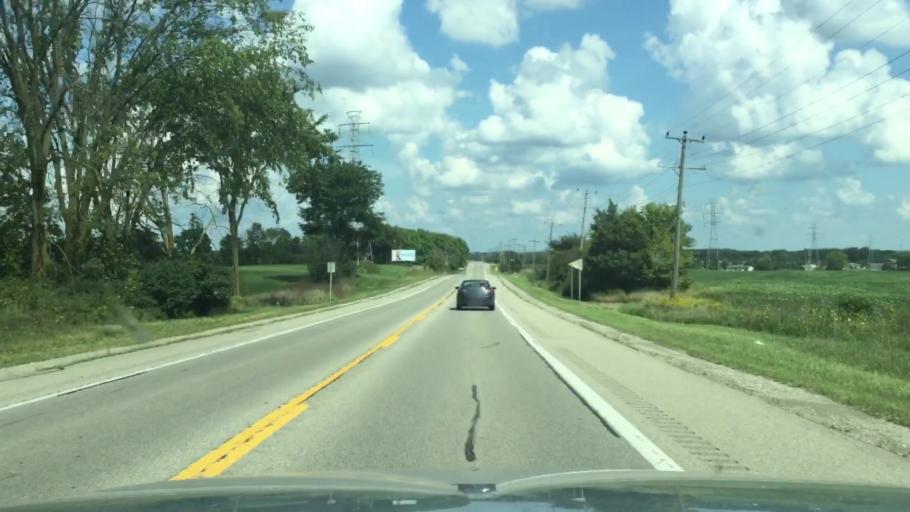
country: US
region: Michigan
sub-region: Washtenaw County
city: Saline
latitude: 42.1536
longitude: -83.8130
